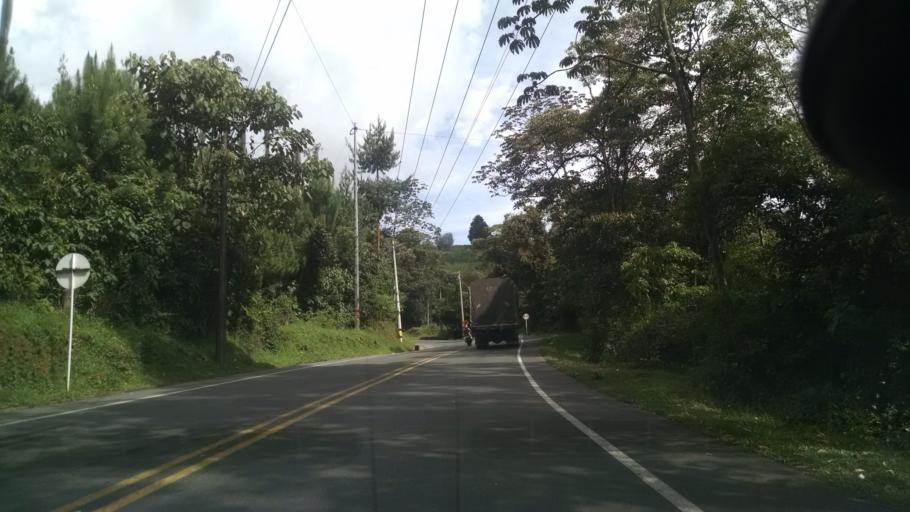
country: CO
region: Antioquia
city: Caldas
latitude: 6.0359
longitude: -75.6254
